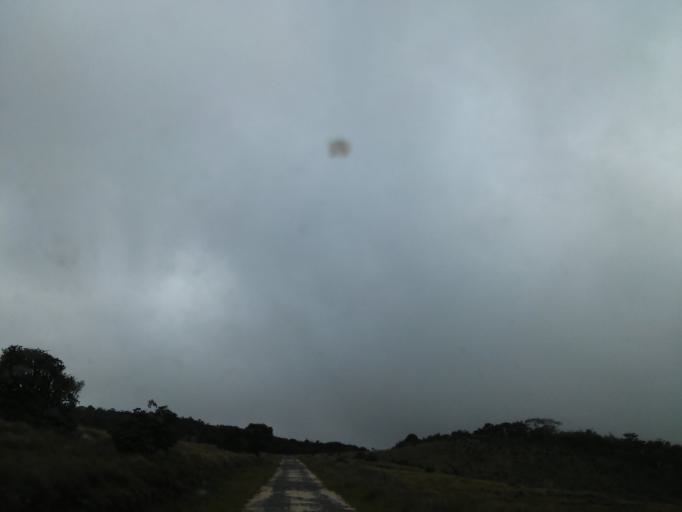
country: LK
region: Uva
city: Haputale
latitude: 6.7953
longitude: 80.8187
